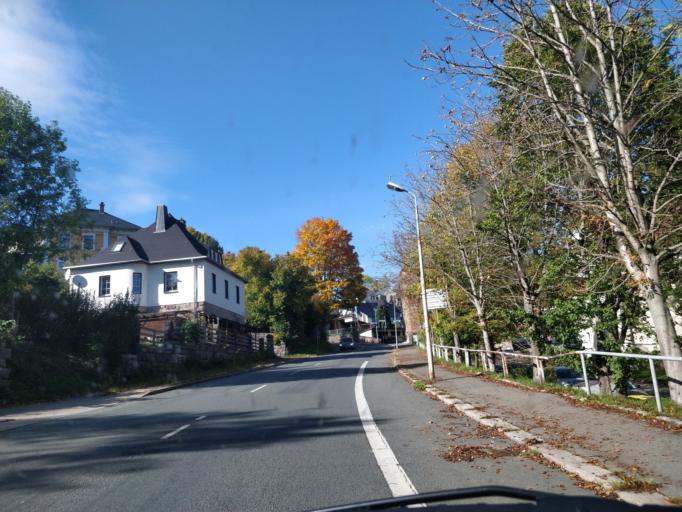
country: DE
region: Saxony
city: Schneeberg
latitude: 50.5982
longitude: 12.6436
